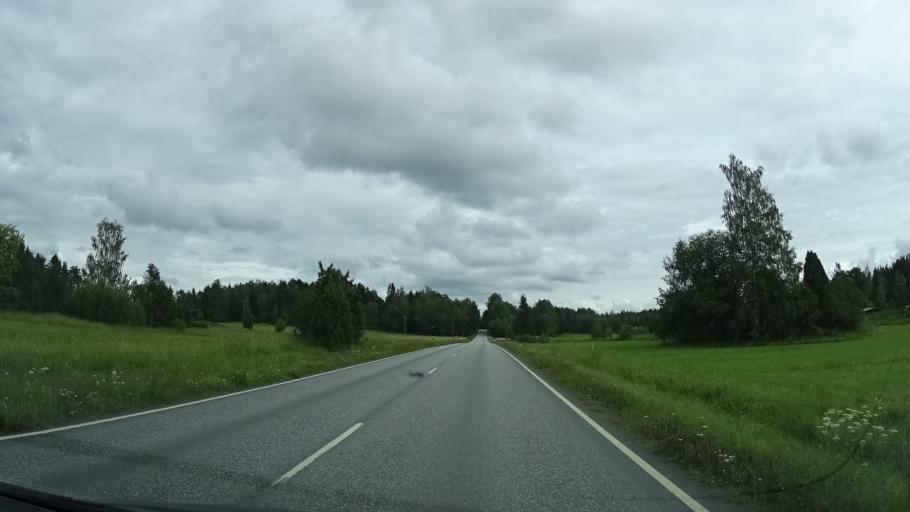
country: FI
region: Pirkanmaa
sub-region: Etelae-Pirkanmaa
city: Urjala
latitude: 61.0875
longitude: 23.4690
